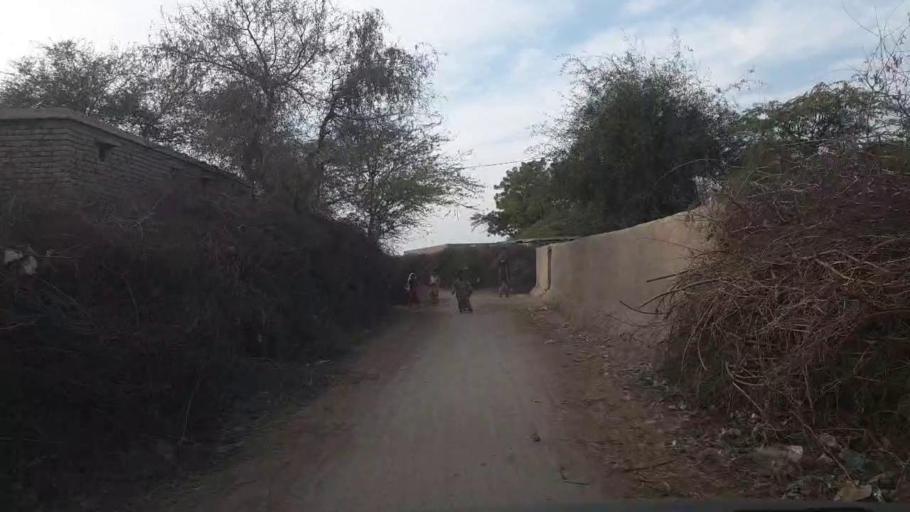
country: PK
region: Sindh
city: Shahpur Chakar
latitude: 26.1228
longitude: 68.5901
